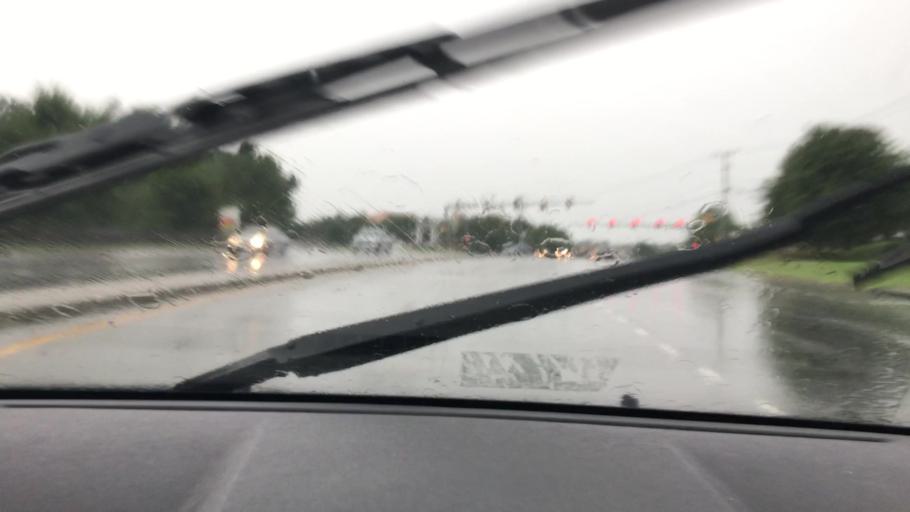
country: US
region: Virginia
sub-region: Henrico County
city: Wyndham
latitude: 37.6803
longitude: -77.5879
